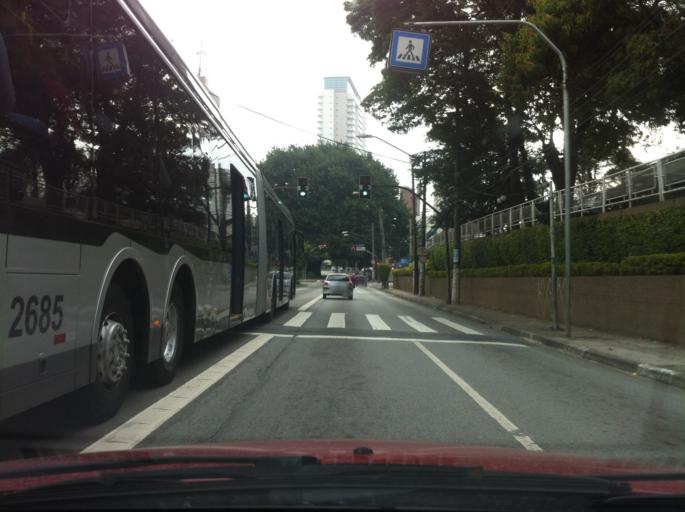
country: BR
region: Sao Paulo
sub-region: Sao Paulo
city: Sao Paulo
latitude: -23.6147
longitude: -46.6791
